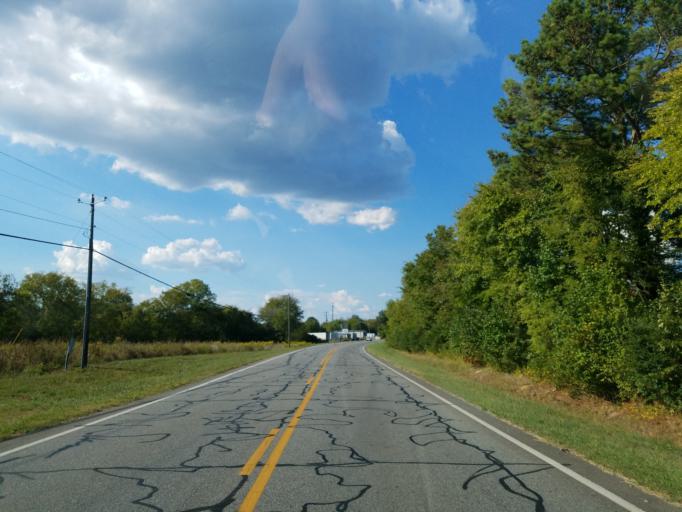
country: US
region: Georgia
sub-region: Bartow County
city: Rydal
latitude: 34.4954
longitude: -84.7090
